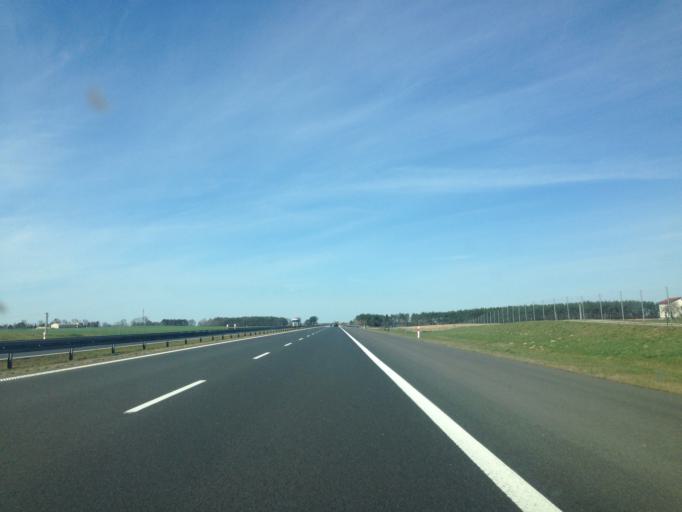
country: PL
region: Pomeranian Voivodeship
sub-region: Powiat starogardzki
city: Smetowo Graniczne
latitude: 53.7761
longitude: 18.6316
